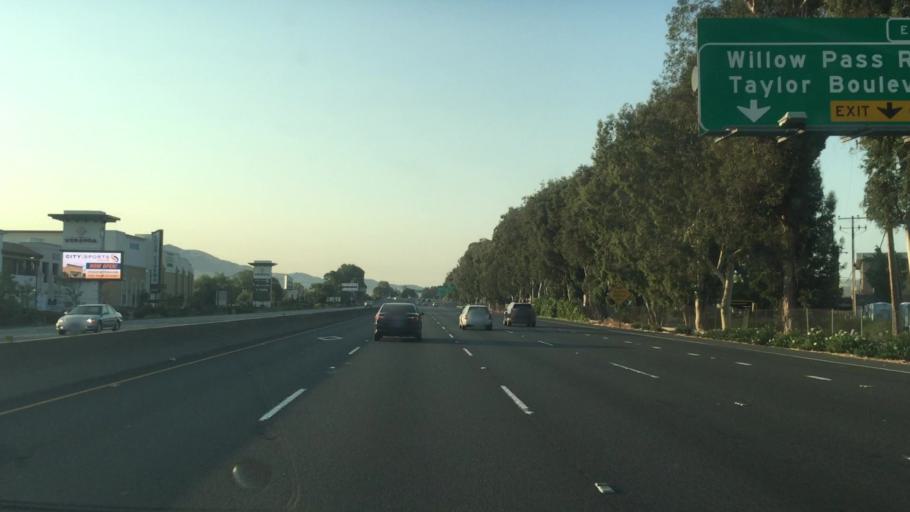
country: US
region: California
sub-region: Contra Costa County
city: Pacheco
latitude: 37.9719
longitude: -122.0610
